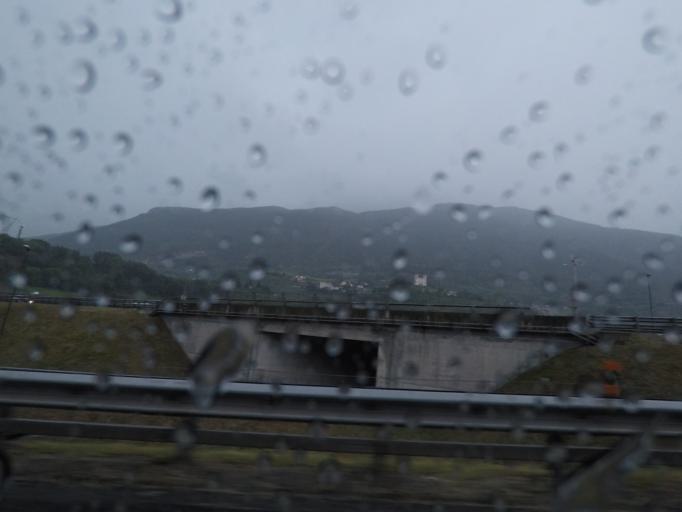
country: IT
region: Aosta Valley
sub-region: Valle d'Aosta
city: Aymavilles
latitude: 45.7080
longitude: 7.2439
